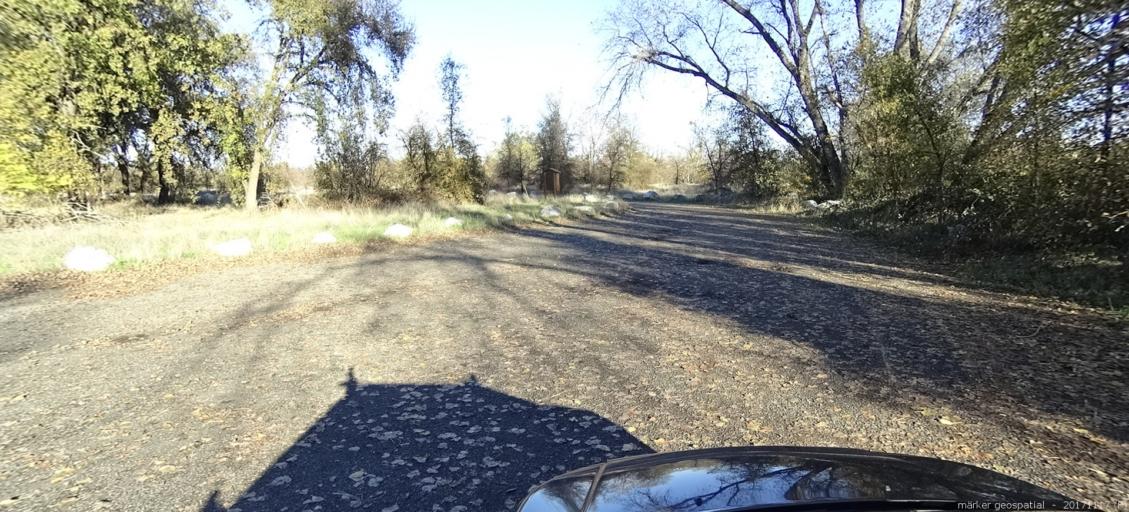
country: US
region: California
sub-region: Shasta County
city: Cottonwood
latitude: 40.3901
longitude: -122.1976
